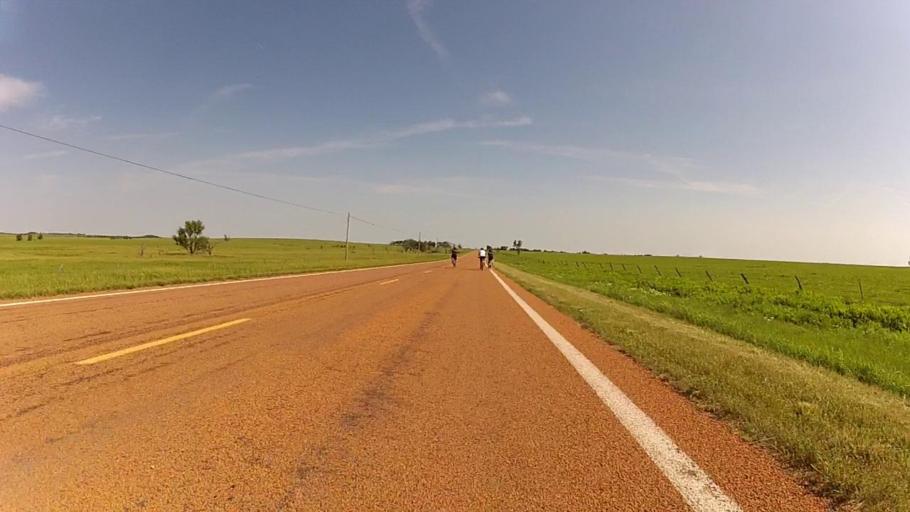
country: US
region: Kansas
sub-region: Cowley County
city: Winfield
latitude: 37.0752
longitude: -96.6436
